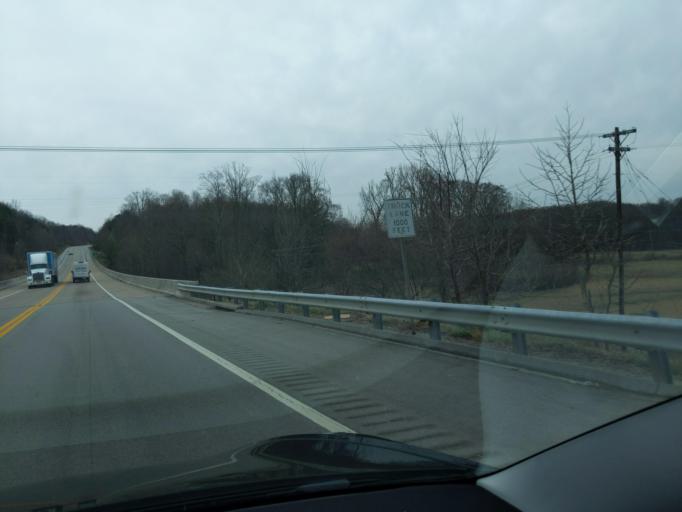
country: US
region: Kentucky
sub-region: Whitley County
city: Corbin
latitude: 36.9163
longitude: -84.0856
